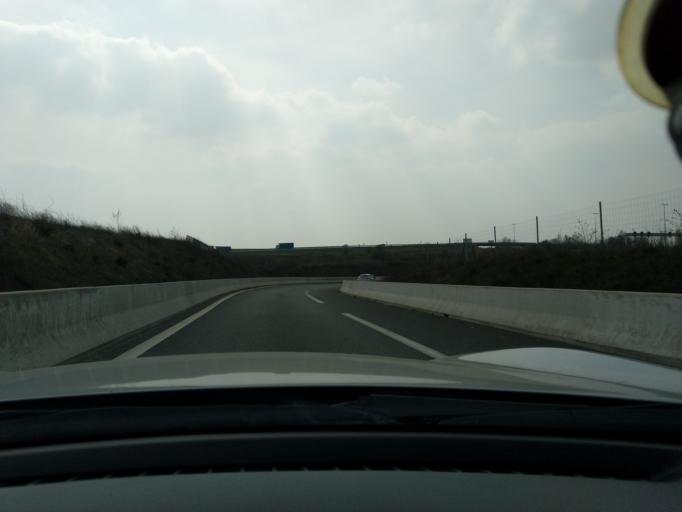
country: FR
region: Ile-de-France
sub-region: Departement du Val-d'Oise
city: Roissy-en-France
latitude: 49.0298
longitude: 2.5410
